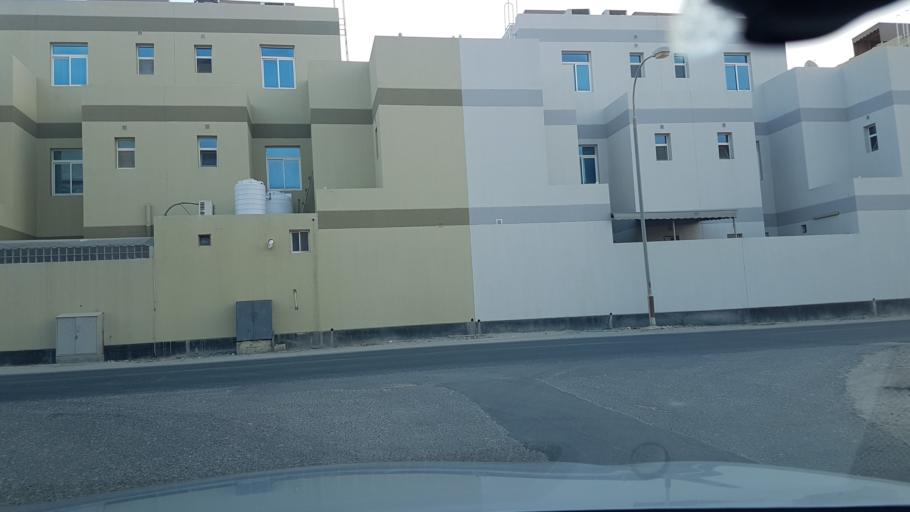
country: BH
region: Manama
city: Jidd Hafs
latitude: 26.2179
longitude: 50.4724
